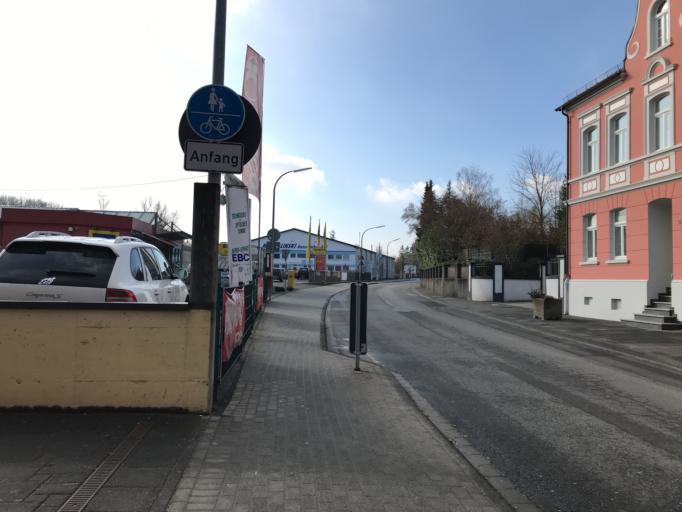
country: DE
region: North Rhine-Westphalia
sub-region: Regierungsbezirk Koln
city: Alfter
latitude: 50.6895
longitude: 7.0229
